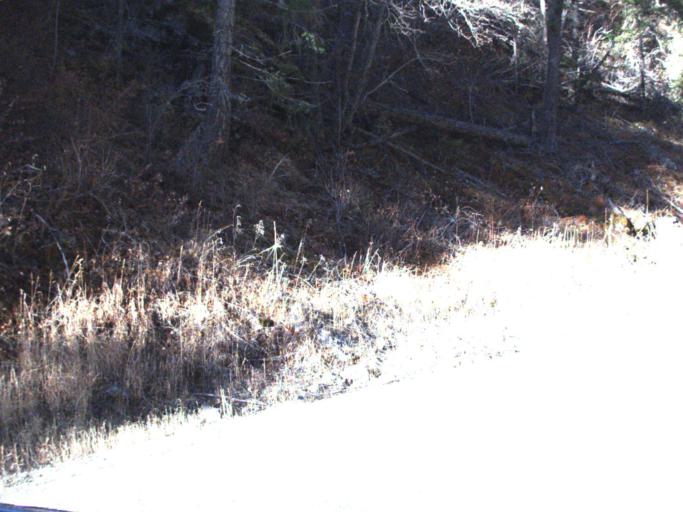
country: US
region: Washington
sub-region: Ferry County
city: Republic
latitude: 48.5423
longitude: -118.7465
